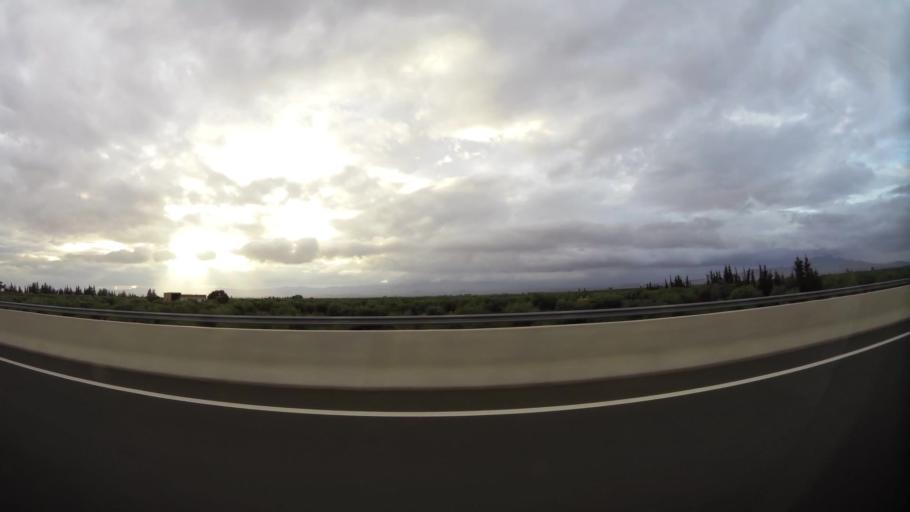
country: MA
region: Taza-Al Hoceima-Taounate
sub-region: Taza
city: Guercif
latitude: 34.3457
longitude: -3.3198
